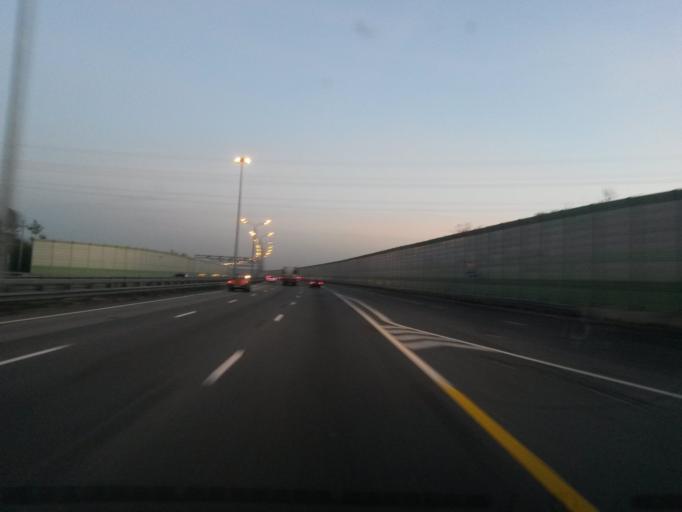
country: RU
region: Moskovskaya
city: Belyye Stolby
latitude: 55.3231
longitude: 37.8117
